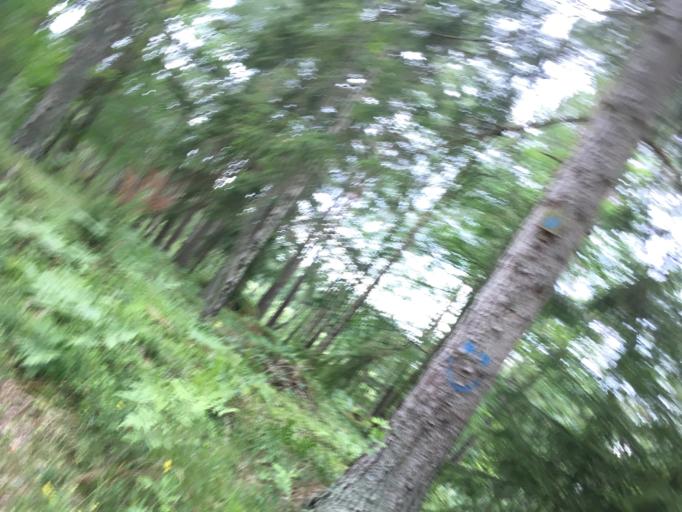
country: SE
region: Kronoberg
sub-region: Vaxjo Kommun
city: Ingelstad
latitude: 56.5912
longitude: 14.7069
